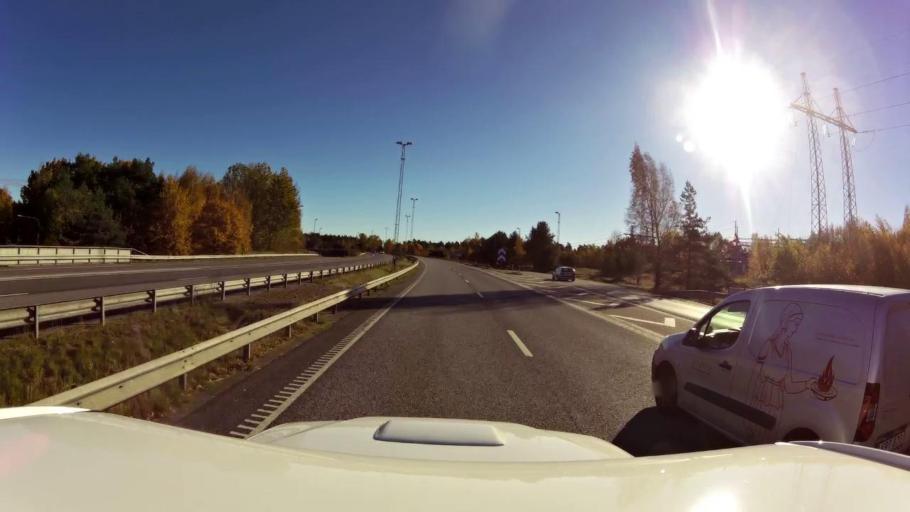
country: SE
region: OEstergoetland
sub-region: Linkopings Kommun
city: Malmslatt
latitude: 58.4063
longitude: 15.5539
